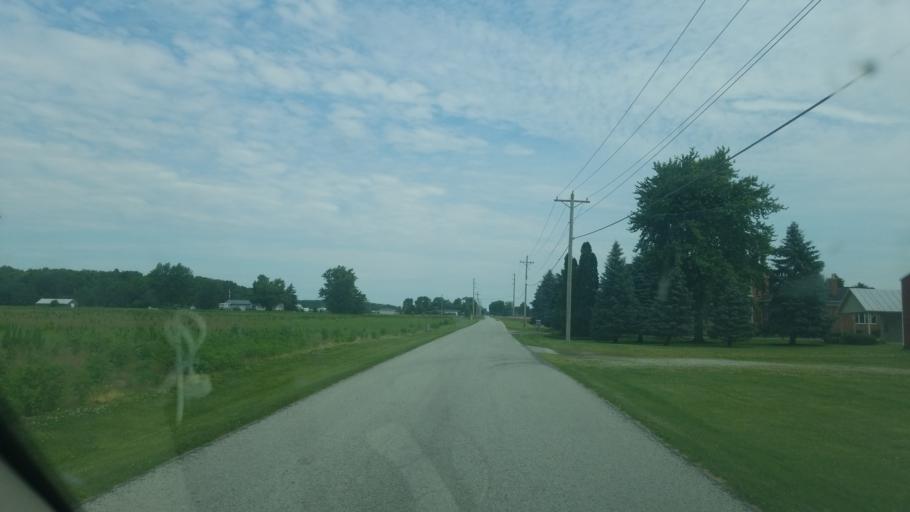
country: US
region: Ohio
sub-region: Seneca County
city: Fostoria
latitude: 41.0596
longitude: -83.4633
